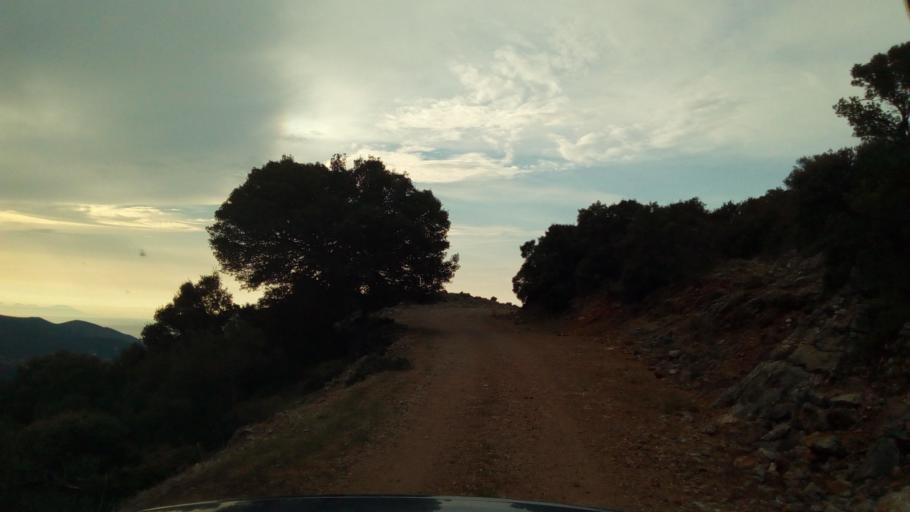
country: GR
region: West Greece
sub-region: Nomos Achaias
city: Kamarai
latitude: 38.4100
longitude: 22.0466
